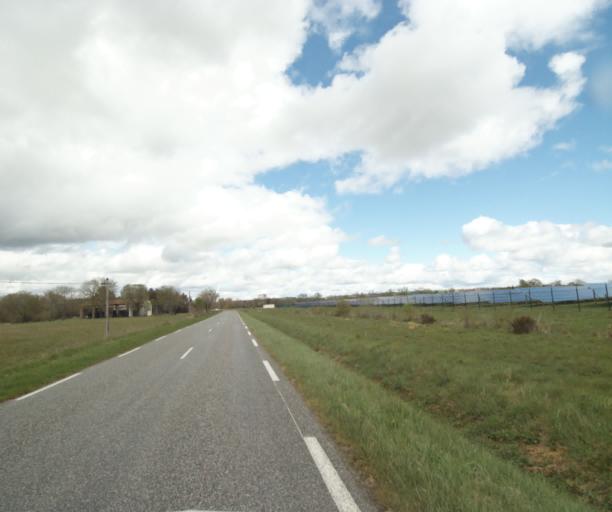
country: FR
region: Midi-Pyrenees
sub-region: Departement de l'Ariege
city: Mazeres
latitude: 43.2395
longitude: 1.6365
